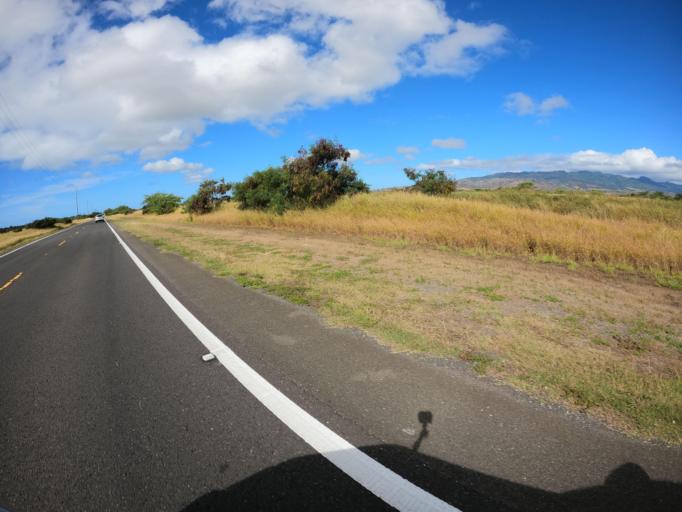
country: US
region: Hawaii
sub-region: Honolulu County
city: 'Ewa Gentry
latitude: 21.3442
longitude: -158.0113
